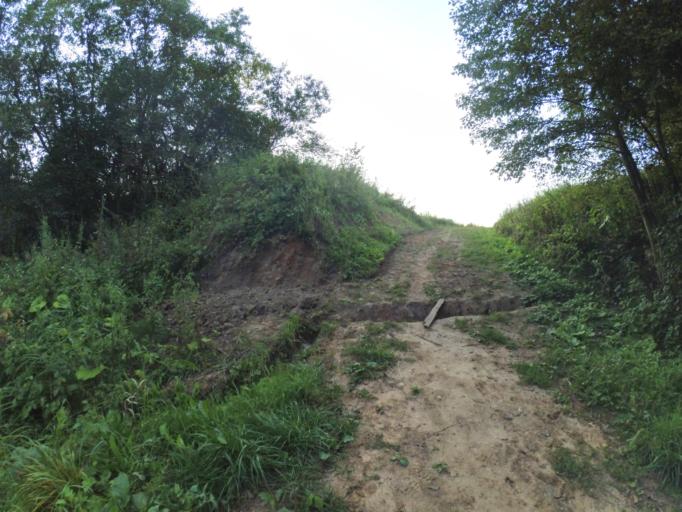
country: RU
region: Moscow
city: Khimki
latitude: 55.8613
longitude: 37.4079
